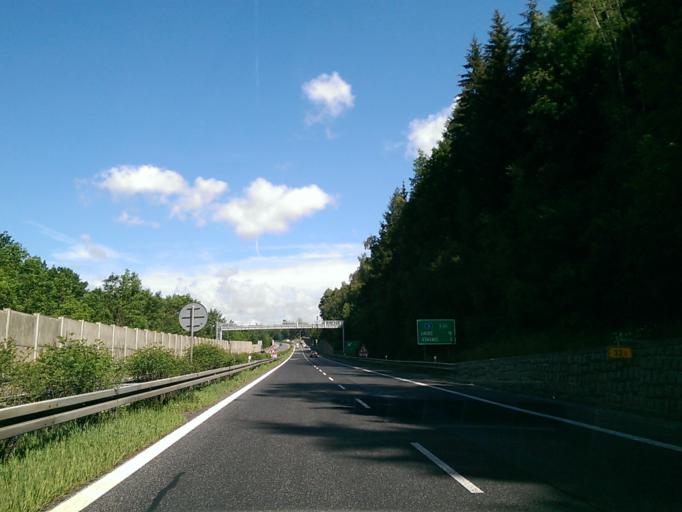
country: CZ
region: Liberecky
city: Hodkovice nad Mohelkou
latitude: 50.6918
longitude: 15.1072
